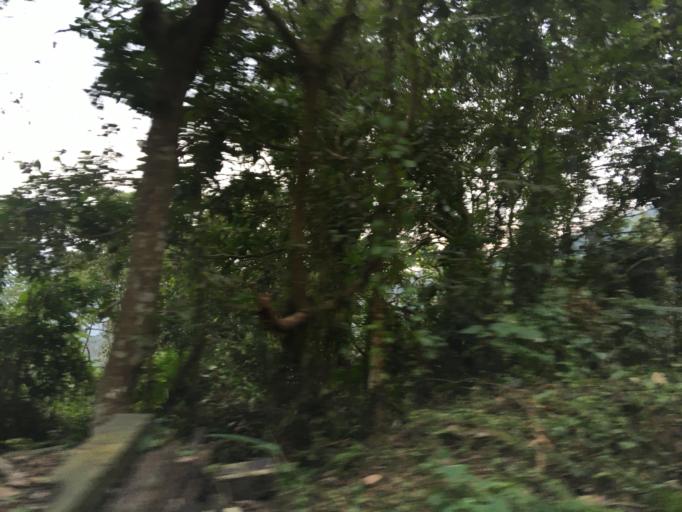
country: TW
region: Taiwan
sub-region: Chiayi
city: Jiayi Shi
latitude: 23.5368
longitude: 120.6066
